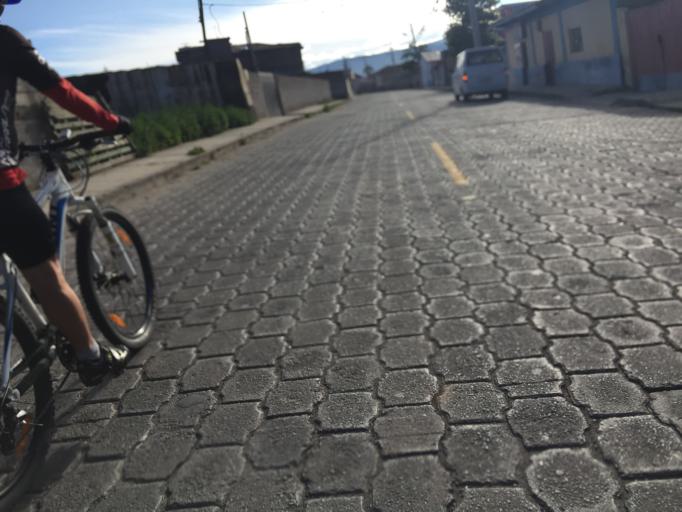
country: EC
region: Imbabura
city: Atuntaqui
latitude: 0.3373
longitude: -78.1985
